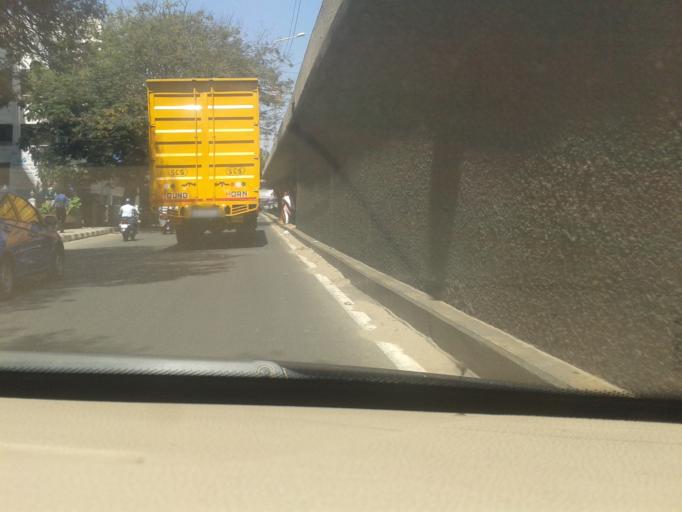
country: IN
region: Karnataka
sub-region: Bangalore Urban
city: Bangalore
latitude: 12.9606
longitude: 77.5939
